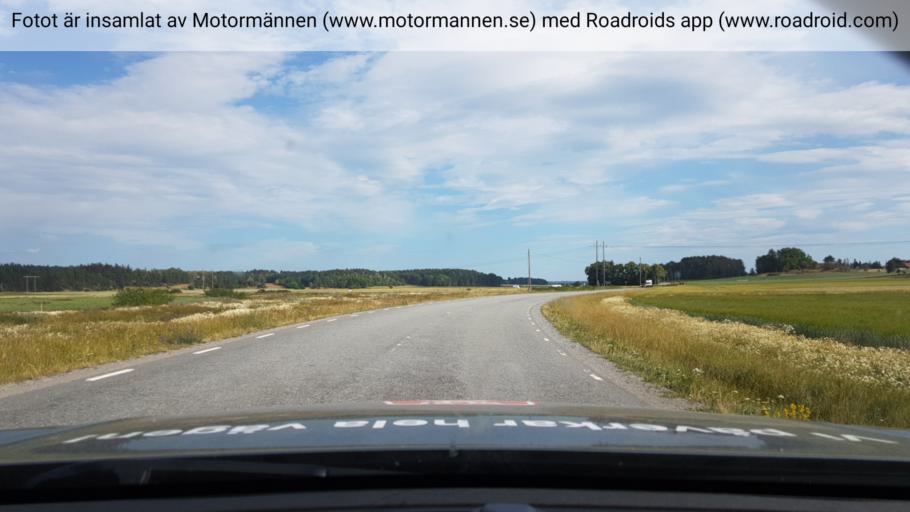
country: SE
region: Uppsala
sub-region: Enkopings Kommun
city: Grillby
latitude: 59.6558
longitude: 17.2543
